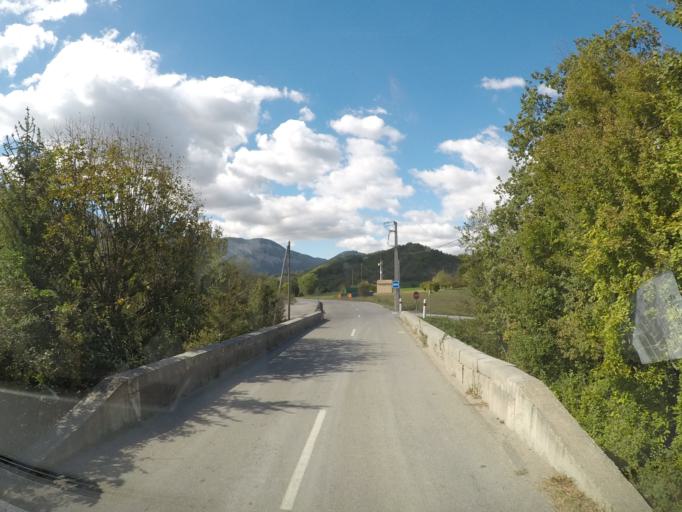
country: FR
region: Provence-Alpes-Cote d'Azur
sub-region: Departement des Hautes-Alpes
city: Laragne-Monteglin
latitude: 44.1696
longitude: 5.7571
